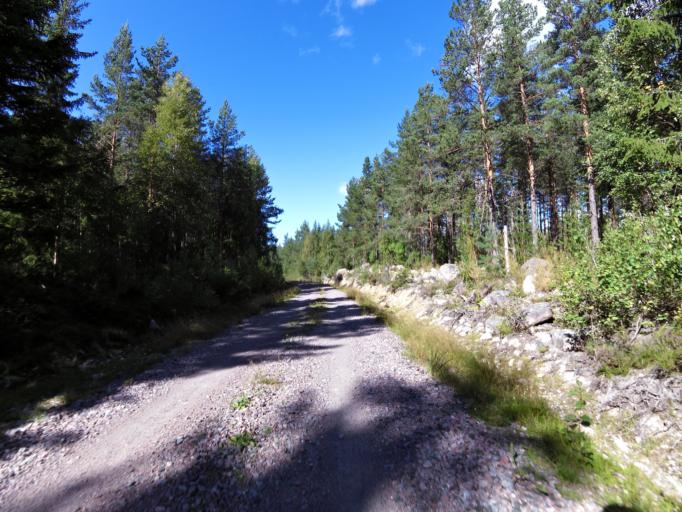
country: SE
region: Gaevleborg
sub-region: Gavle Kommun
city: Valbo
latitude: 60.7287
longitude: 16.9983
